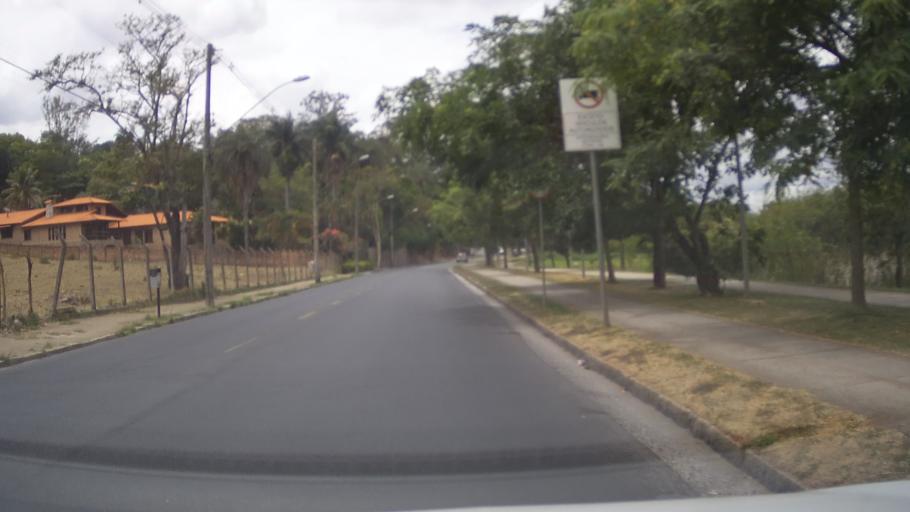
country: BR
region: Minas Gerais
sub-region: Contagem
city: Contagem
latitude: -19.8508
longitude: -44.0036
